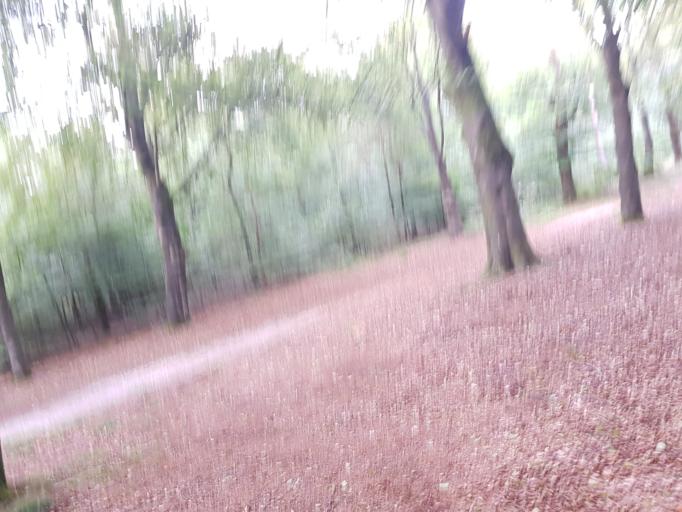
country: NL
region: Utrecht
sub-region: Gemeente Rhenen
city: Rhenen
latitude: 51.9845
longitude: 5.5508
